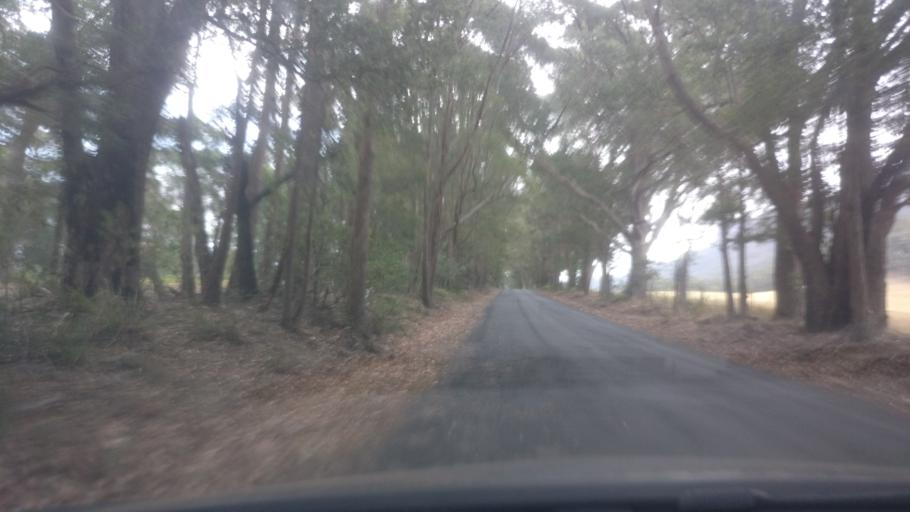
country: AU
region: New South Wales
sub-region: Shoalhaven Shire
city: Kangaroo Valley
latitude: -34.7213
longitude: 150.4699
